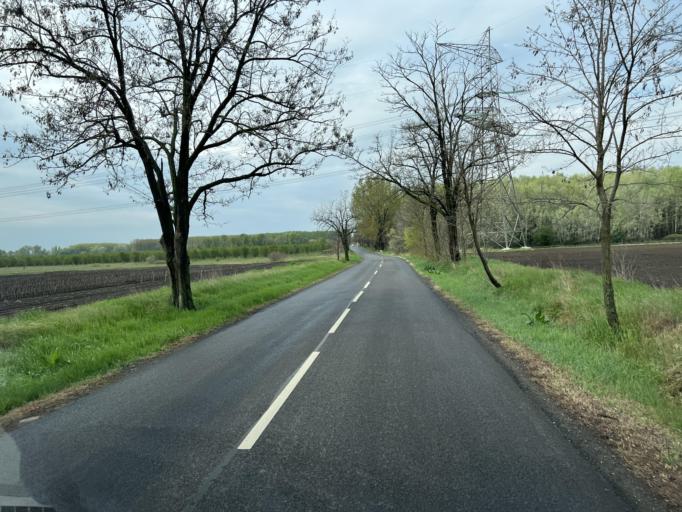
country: HU
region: Pest
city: Danszentmiklos
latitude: 47.2205
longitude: 19.5781
